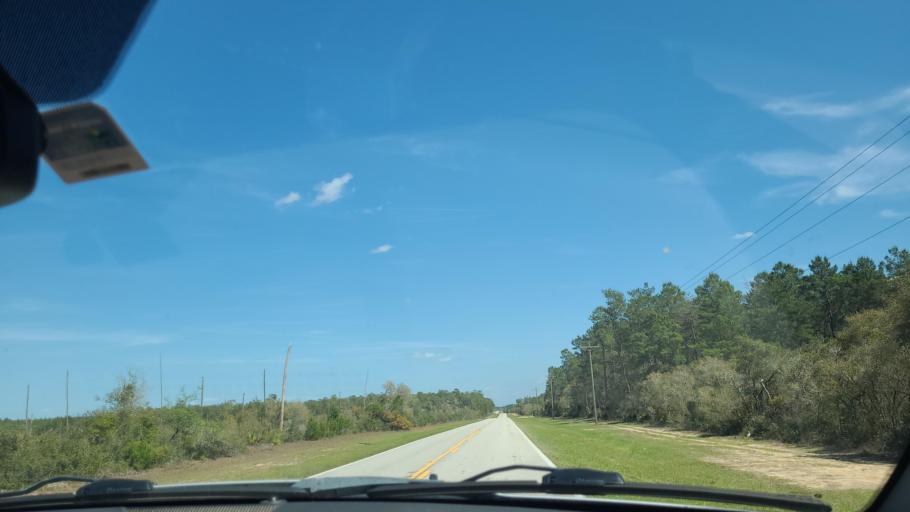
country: US
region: Florida
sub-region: Marion County
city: Citra
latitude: 29.3675
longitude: -81.8622
